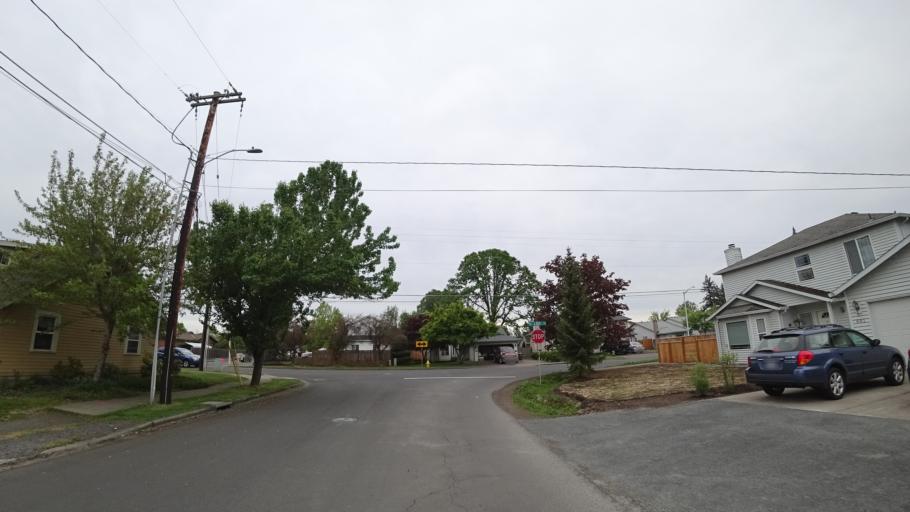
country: US
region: Oregon
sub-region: Washington County
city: Aloha
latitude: 45.5126
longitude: -122.9145
